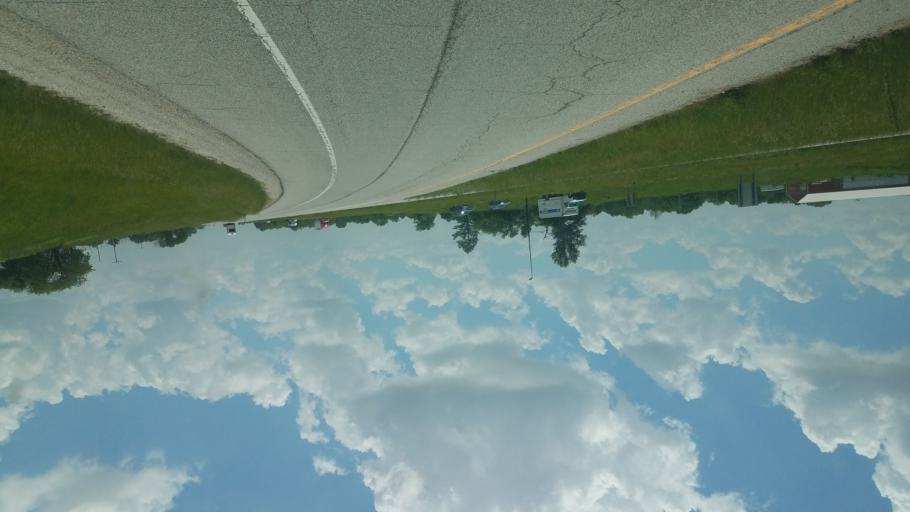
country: US
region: Illinois
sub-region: Bond County
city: Greenville
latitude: 38.8308
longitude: -89.5484
